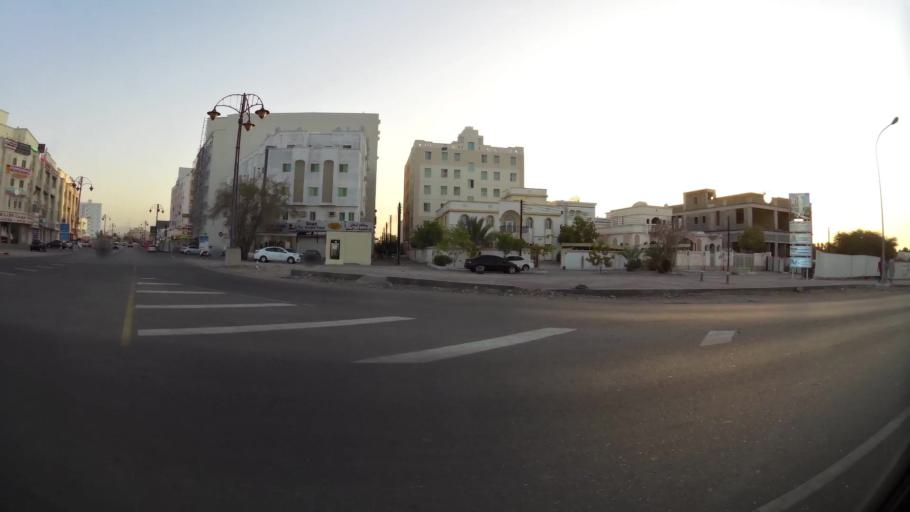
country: OM
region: Muhafazat Masqat
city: As Sib al Jadidah
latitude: 23.6418
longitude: 58.2054
